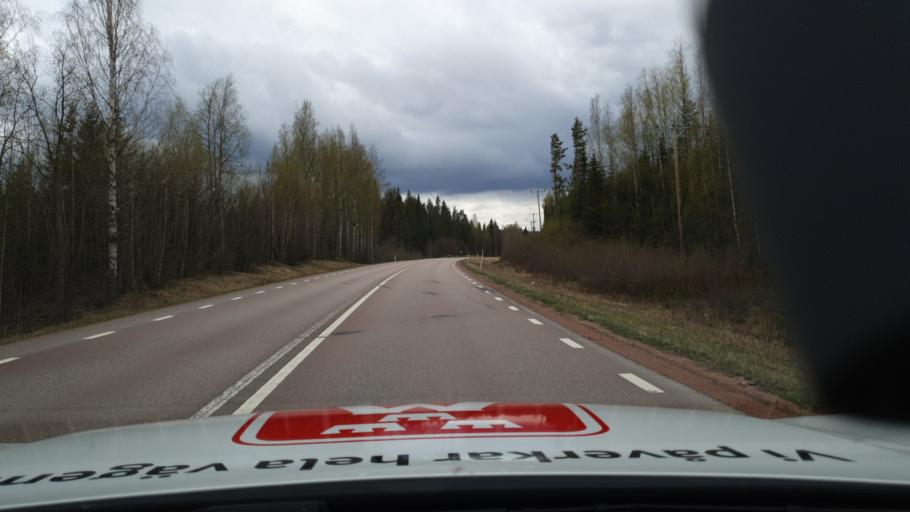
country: SE
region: Jaemtland
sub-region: Ragunda Kommun
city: Hammarstrand
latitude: 63.1658
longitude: 15.8058
